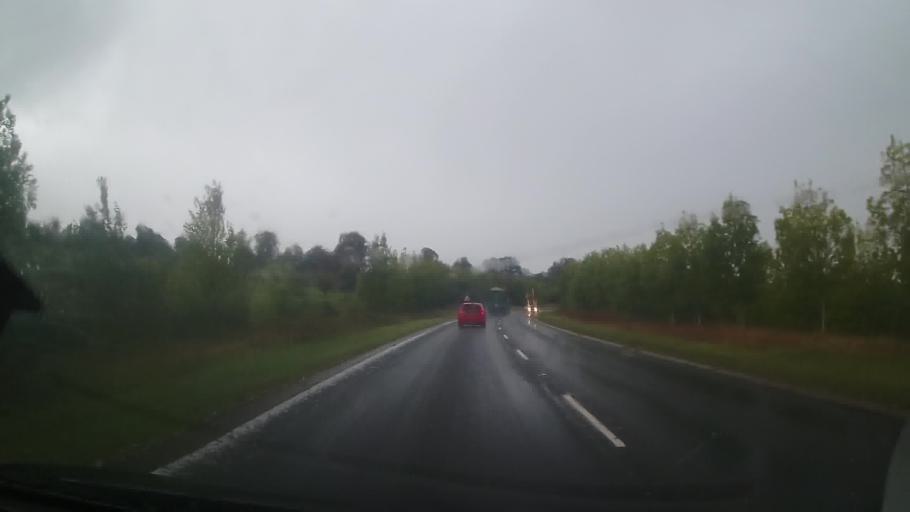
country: GB
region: England
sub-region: Worcestershire
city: Evesham
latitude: 52.1118
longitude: -1.9502
